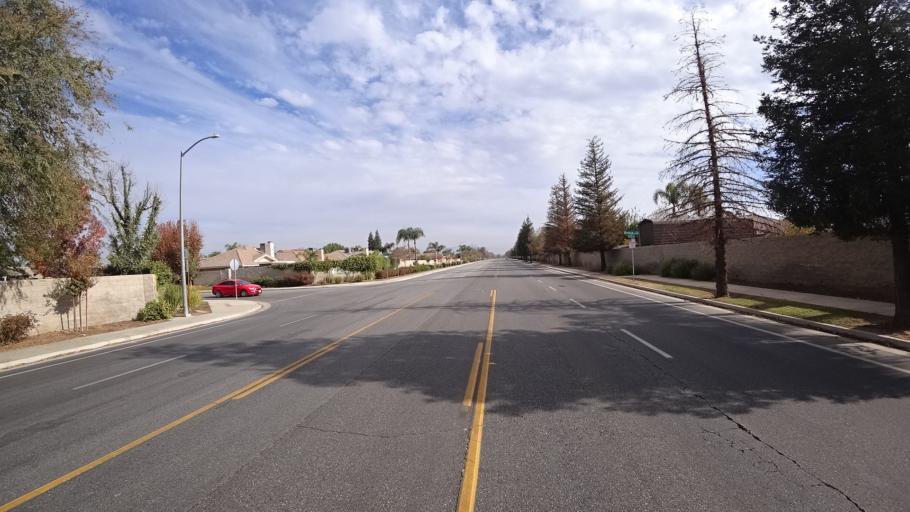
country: US
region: California
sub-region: Kern County
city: Greenacres
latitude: 35.4052
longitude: -119.1250
